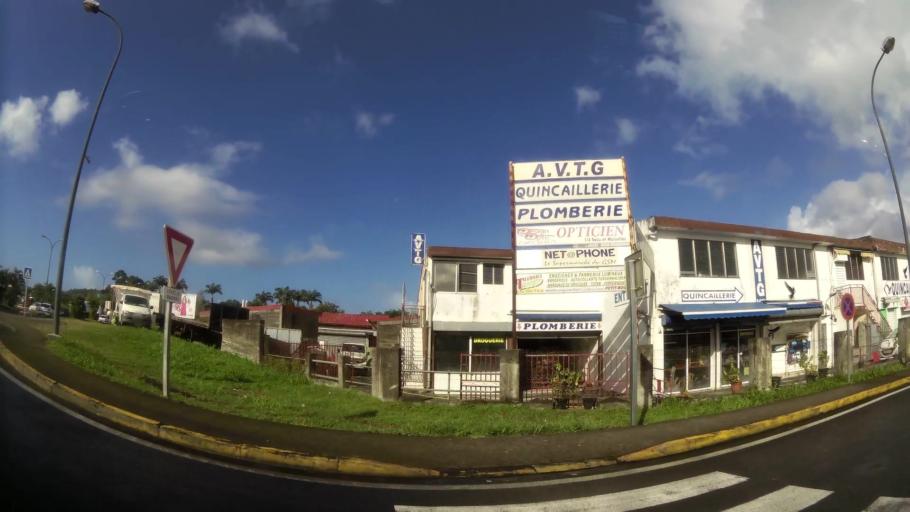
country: MQ
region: Martinique
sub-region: Martinique
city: Ducos
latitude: 14.5247
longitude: -60.9809
